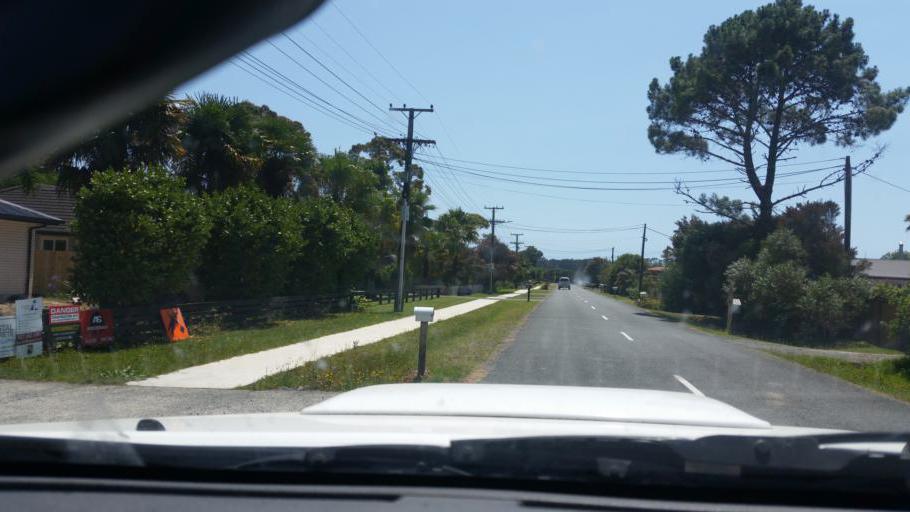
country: NZ
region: Auckland
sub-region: Auckland
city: Wellsford
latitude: -36.1229
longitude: 174.5745
